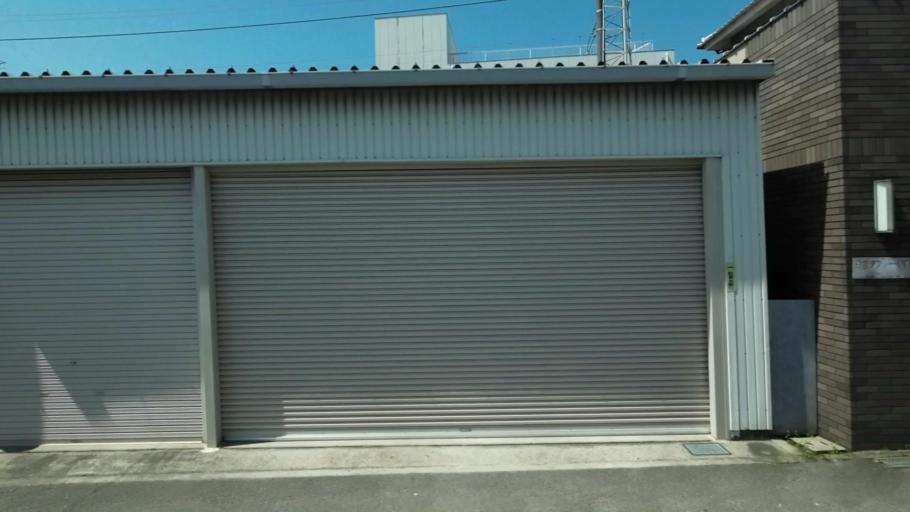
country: JP
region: Ehime
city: Hojo
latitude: 34.0675
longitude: 132.9910
